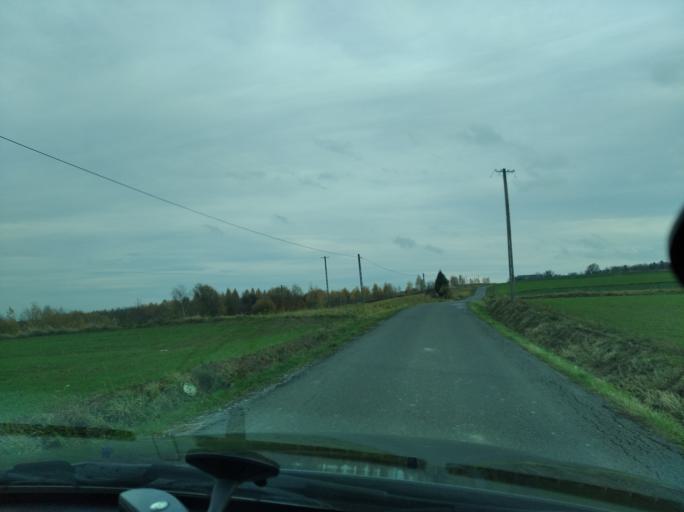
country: PL
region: Subcarpathian Voivodeship
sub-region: Powiat strzyzowski
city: Strzyzow
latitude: 49.9151
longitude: 21.7672
